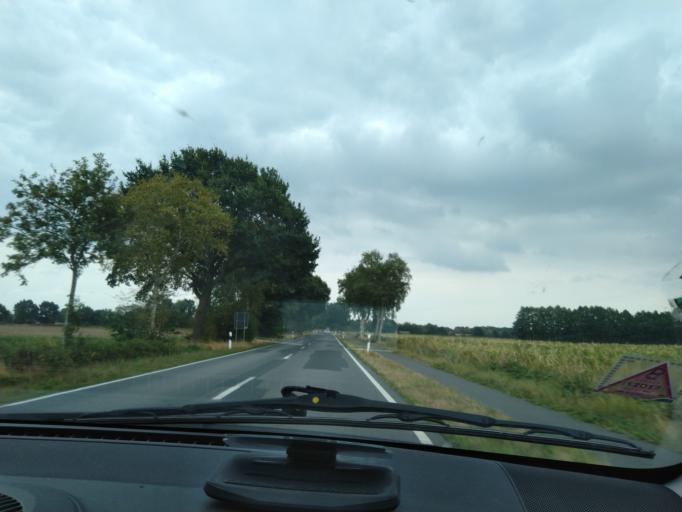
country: DE
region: Lower Saxony
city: Rhede
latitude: 53.0677
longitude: 7.2151
